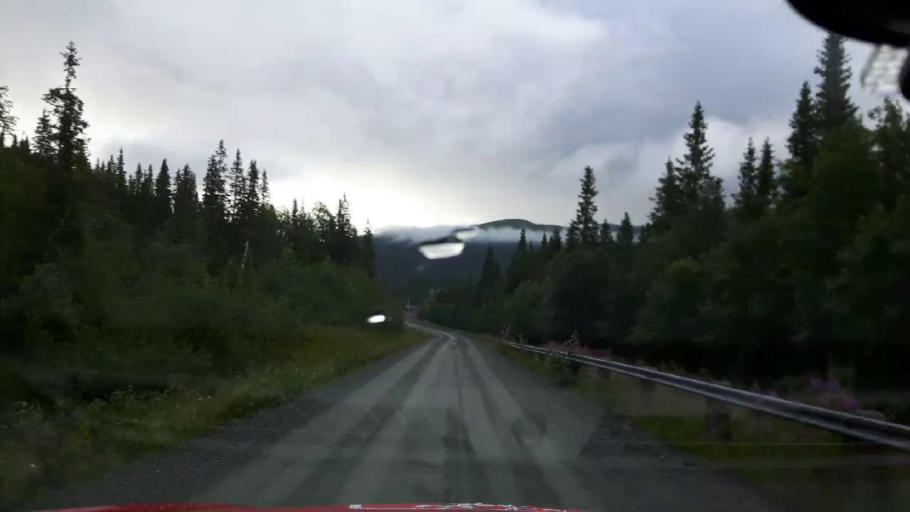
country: NO
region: Nordland
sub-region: Hattfjelldal
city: Hattfjelldal
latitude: 64.8841
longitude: 14.7682
